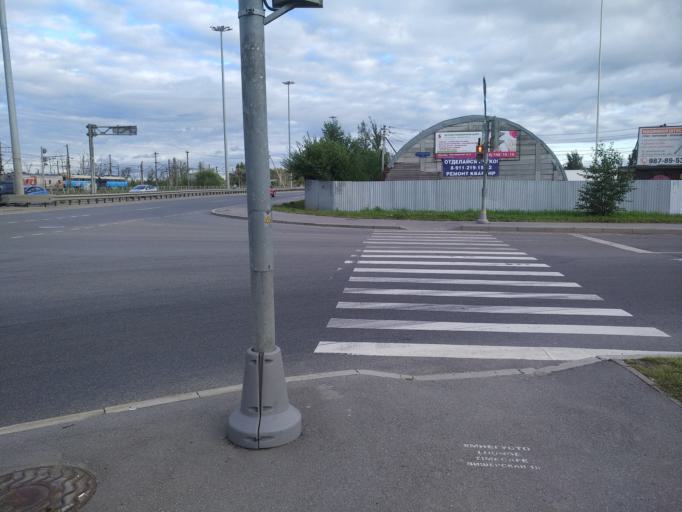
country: RU
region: St.-Petersburg
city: Shushary
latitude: 59.8046
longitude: 30.3875
